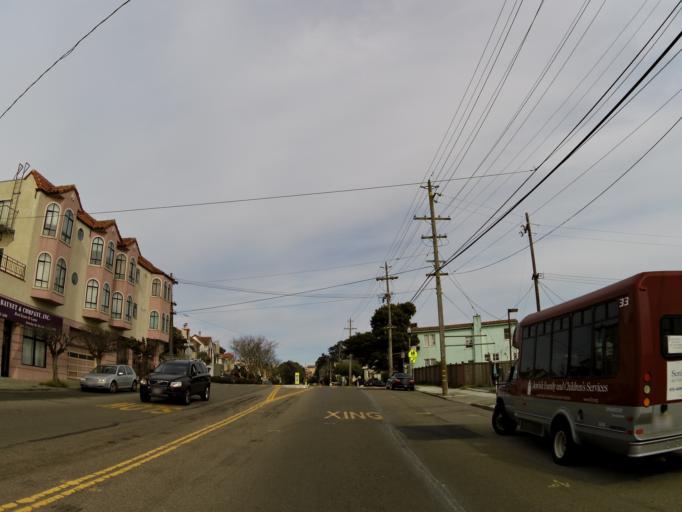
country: US
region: California
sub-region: San Mateo County
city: Daly City
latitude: 37.7433
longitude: -122.4687
